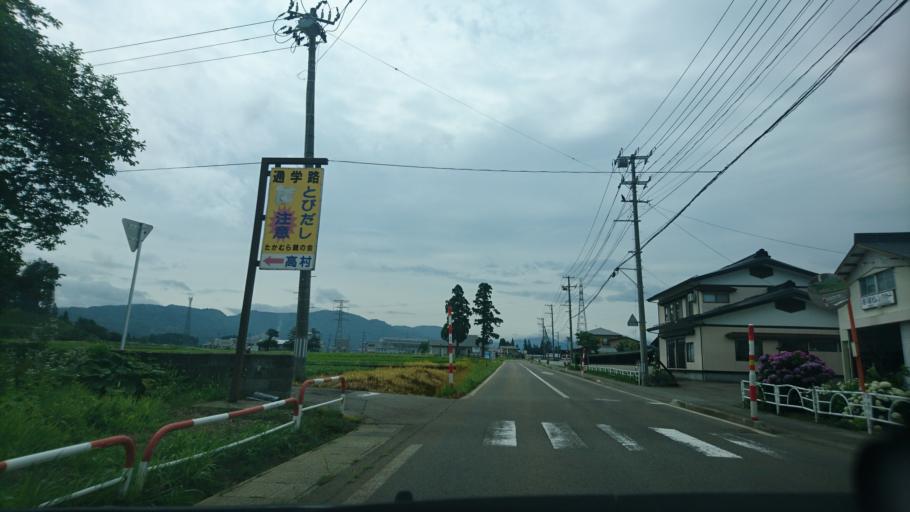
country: JP
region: Akita
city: Yuzawa
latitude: 39.1835
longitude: 140.5537
